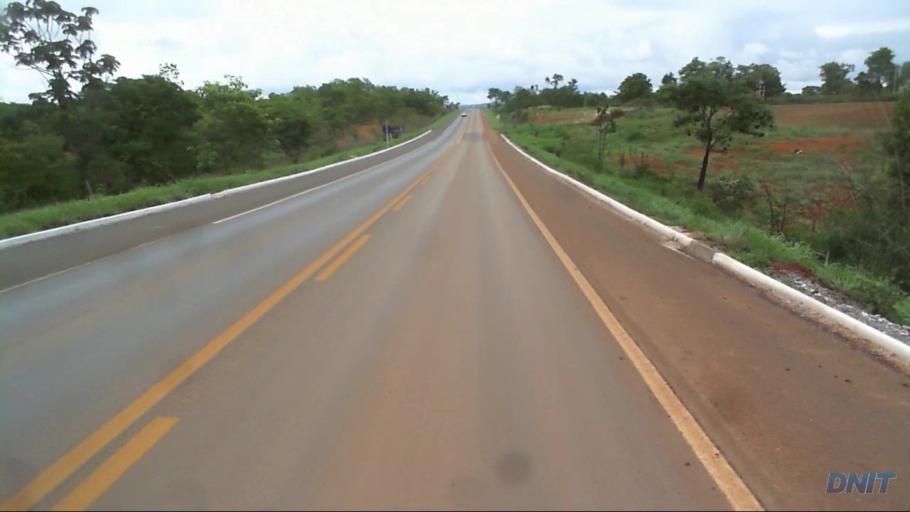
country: BR
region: Goias
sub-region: Padre Bernardo
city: Padre Bernardo
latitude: -15.1526
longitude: -48.3329
